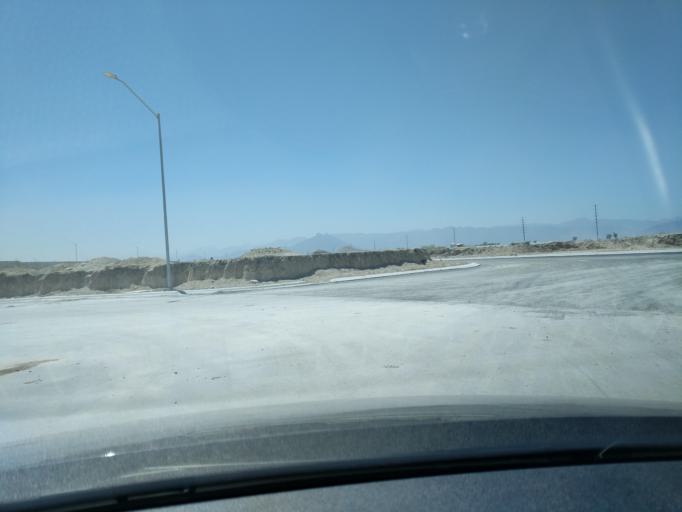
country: MX
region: Nuevo Leon
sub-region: Apodaca
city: Artemio Trevino
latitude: 25.8447
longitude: -100.1447
